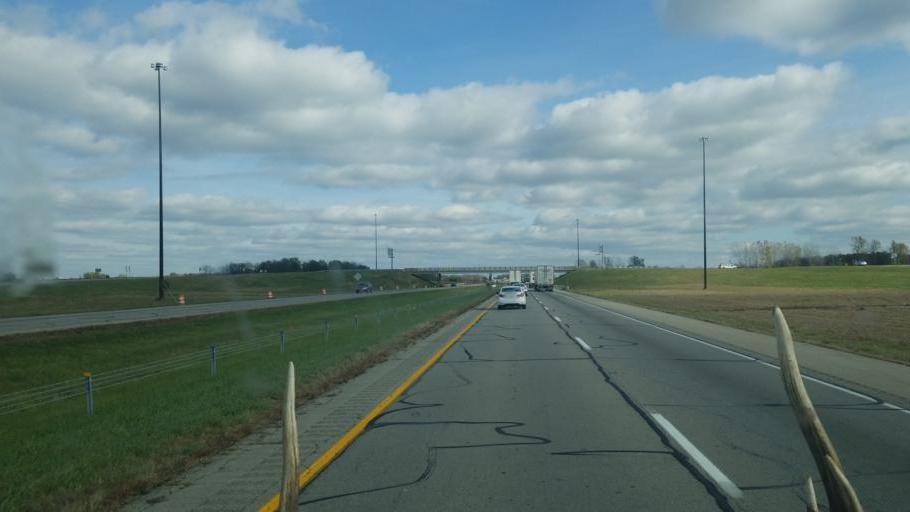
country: US
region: Indiana
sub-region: Wayne County
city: Cambridge City
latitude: 39.8520
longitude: -85.2660
